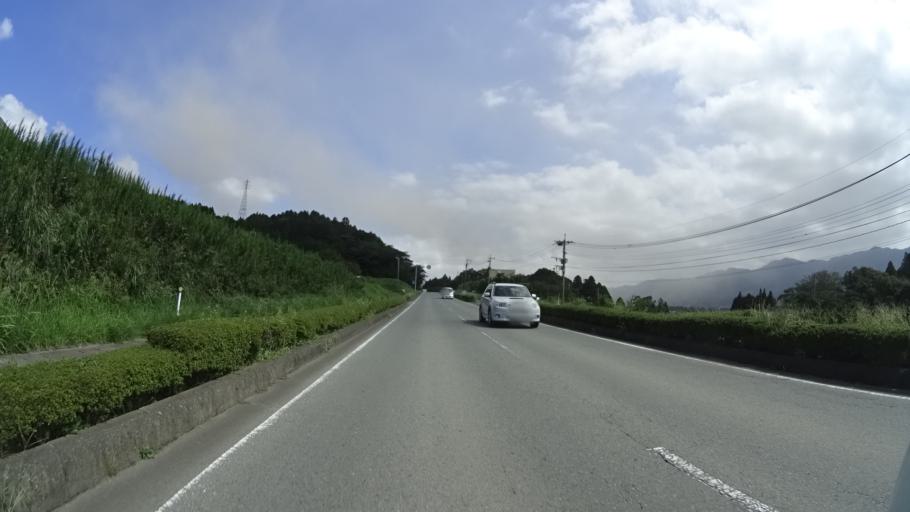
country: JP
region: Kumamoto
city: Aso
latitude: 32.8461
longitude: 131.0355
